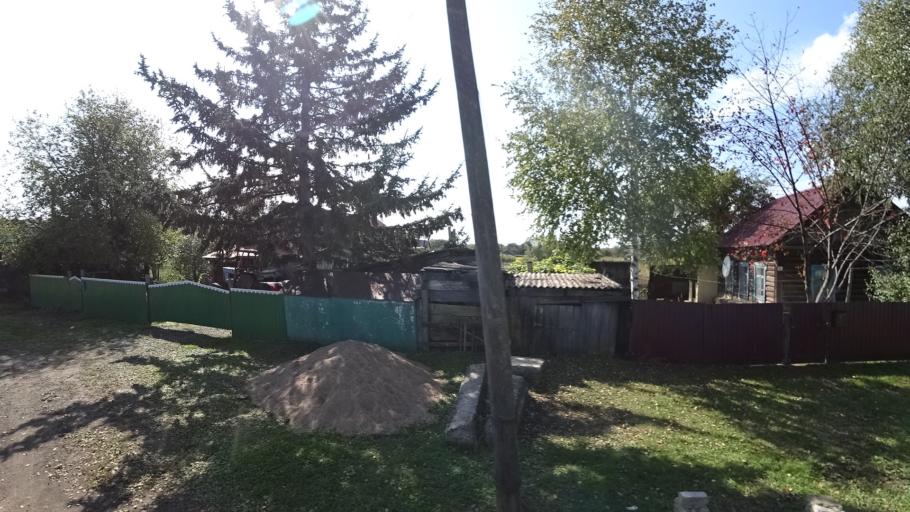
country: RU
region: Amur
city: Arkhara
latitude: 49.4015
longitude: 130.1449
